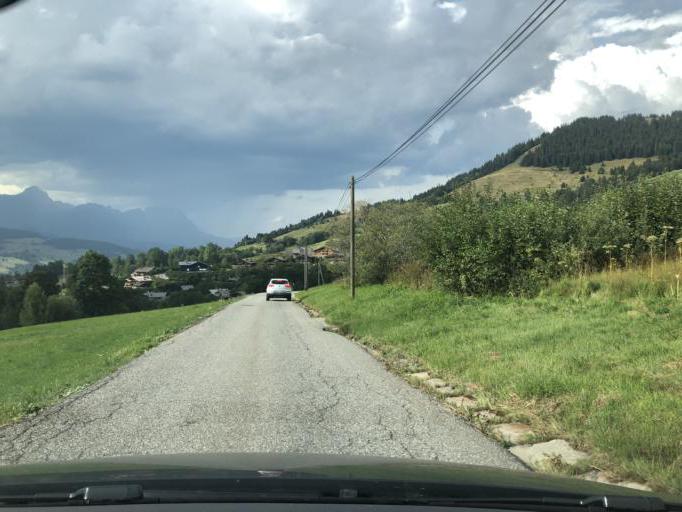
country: FR
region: Rhone-Alpes
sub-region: Departement de la Haute-Savoie
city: Megeve
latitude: 45.8416
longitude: 6.6427
